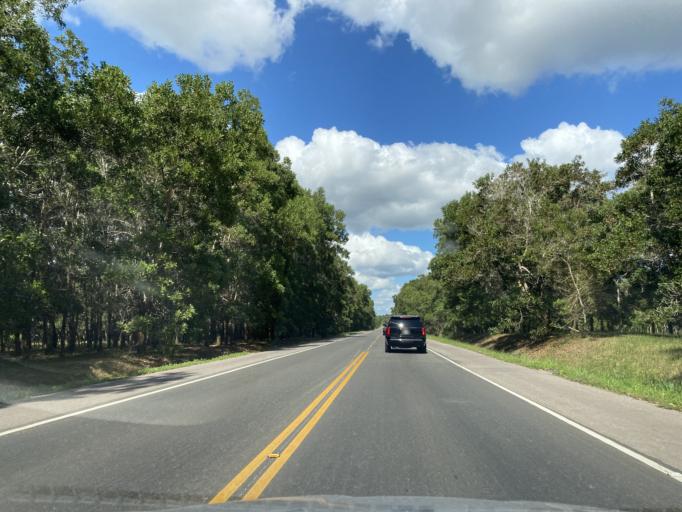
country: DO
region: Monte Plata
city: Monte Plata
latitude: 18.7517
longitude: -69.7658
